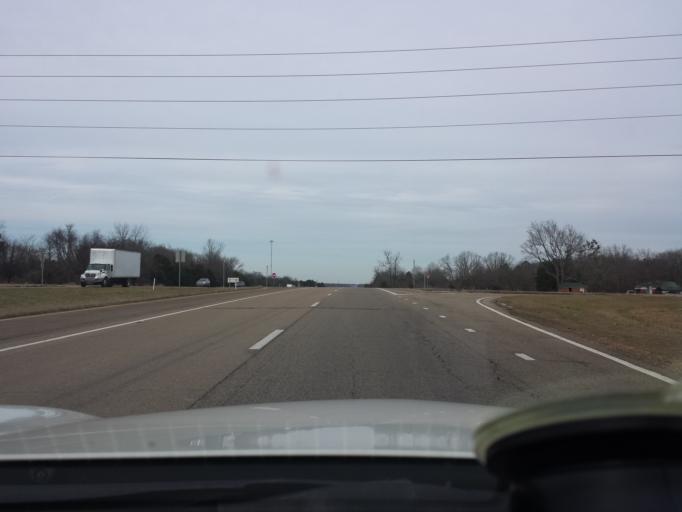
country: US
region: Mississippi
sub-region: Clay County
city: West Point
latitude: 33.5281
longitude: -88.6589
